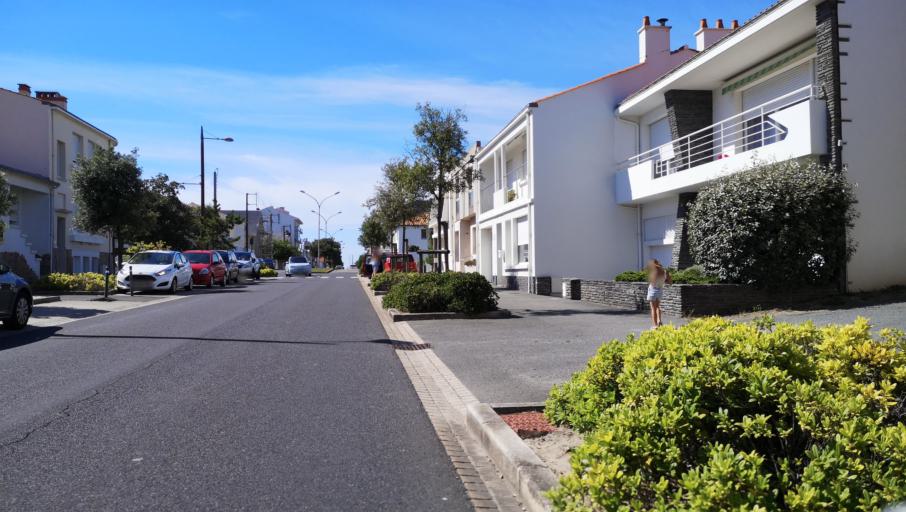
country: FR
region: Pays de la Loire
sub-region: Departement de la Vendee
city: Les Sables-d'Olonne
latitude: 46.4905
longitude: -1.7679
